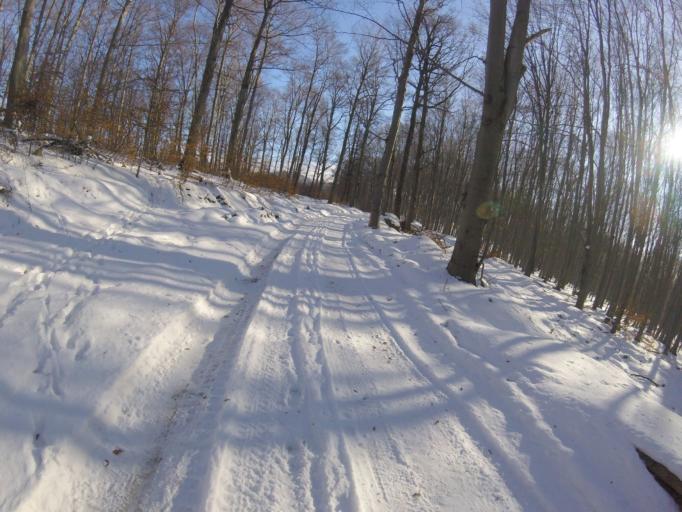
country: HU
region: Pest
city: Szob
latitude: 47.9527
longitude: 18.8903
